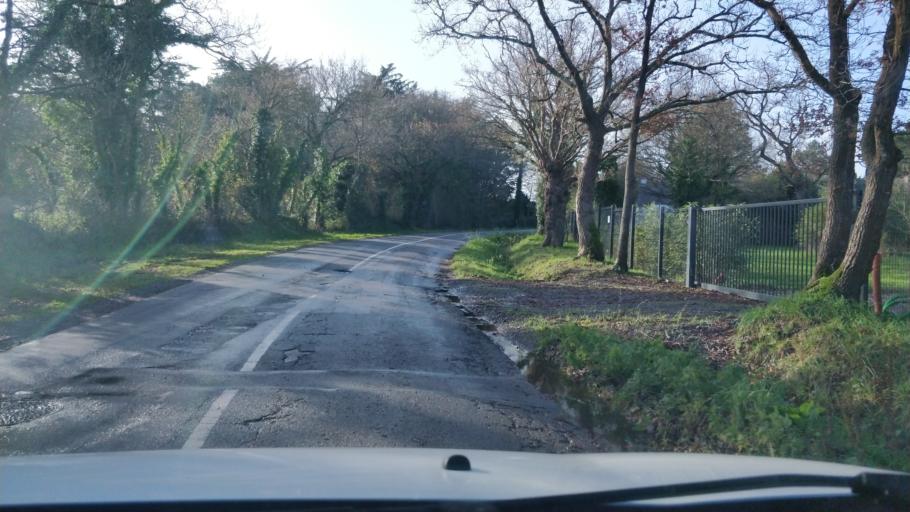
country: FR
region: Pays de la Loire
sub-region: Departement de la Loire-Atlantique
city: Mesquer
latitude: 47.3955
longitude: -2.4644
